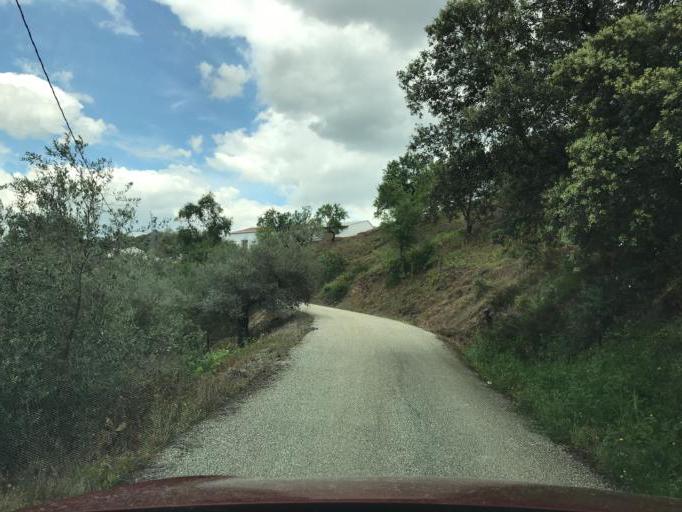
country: ES
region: Andalusia
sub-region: Provincia de Malaga
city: Comares
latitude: 36.8772
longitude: -4.2583
